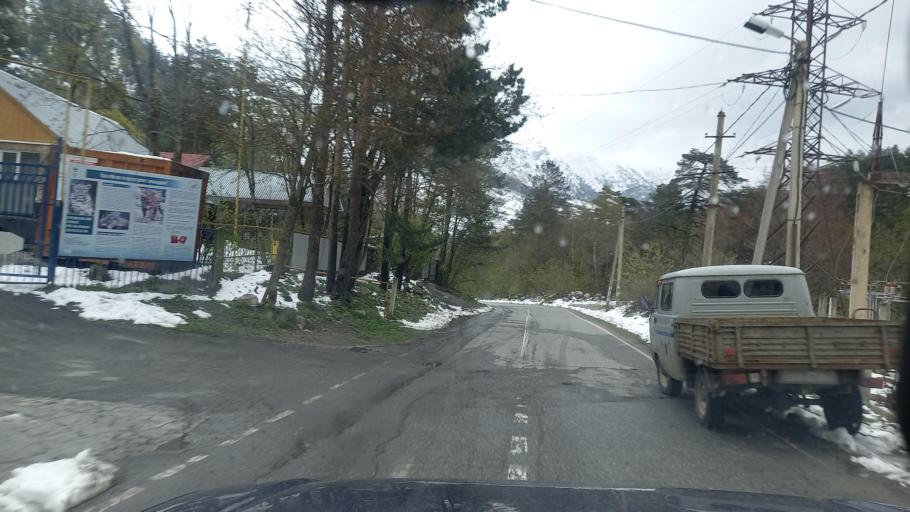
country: RU
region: North Ossetia
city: Mizur
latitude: 42.7931
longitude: 43.9227
